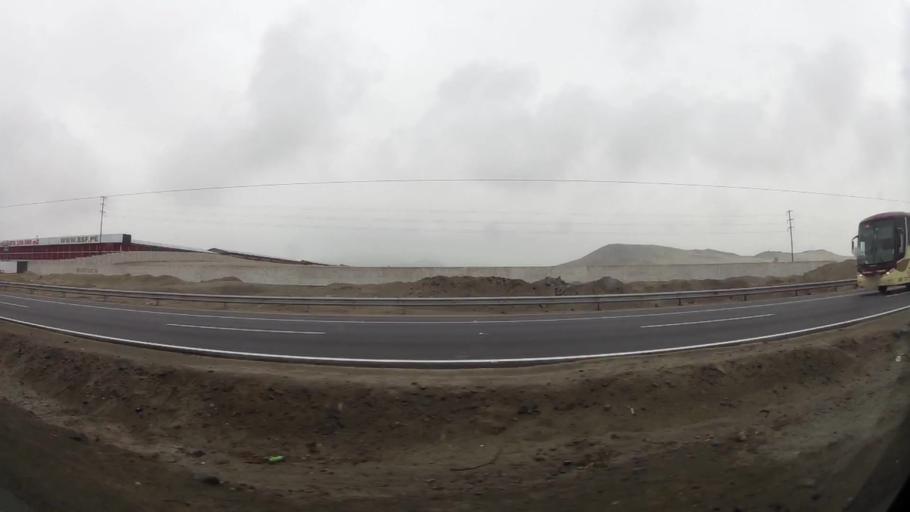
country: PE
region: Lima
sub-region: Lima
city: Punta Hermosa
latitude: -12.3225
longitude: -76.8272
